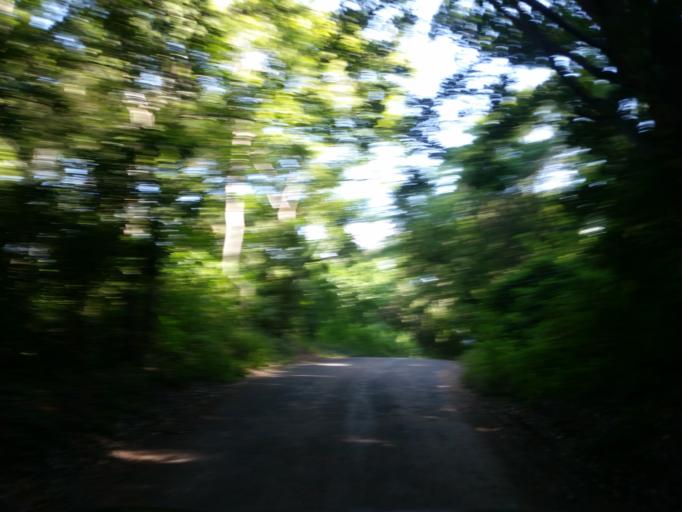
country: NI
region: Masaya
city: Catarina
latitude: 11.9338
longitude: -86.0572
